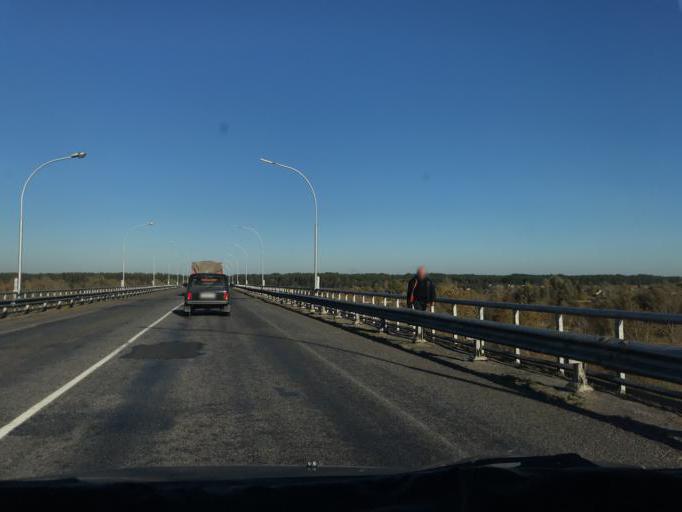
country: BY
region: Gomel
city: Mazyr
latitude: 52.0256
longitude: 29.3225
